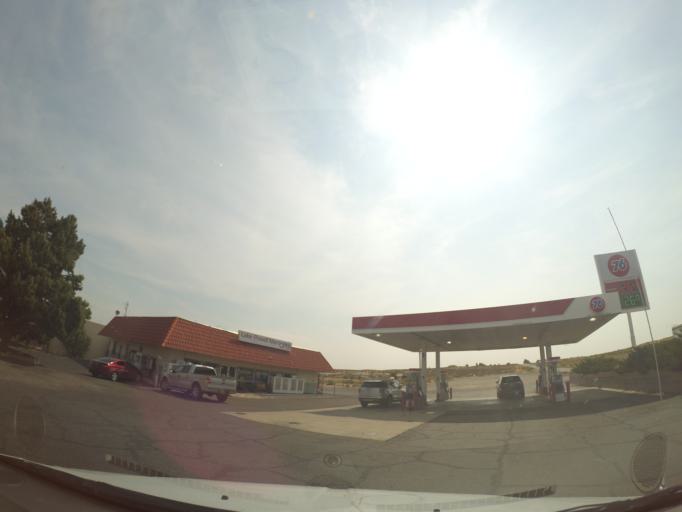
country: US
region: Arizona
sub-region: Coconino County
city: Page
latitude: 36.9954
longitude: -111.5648
